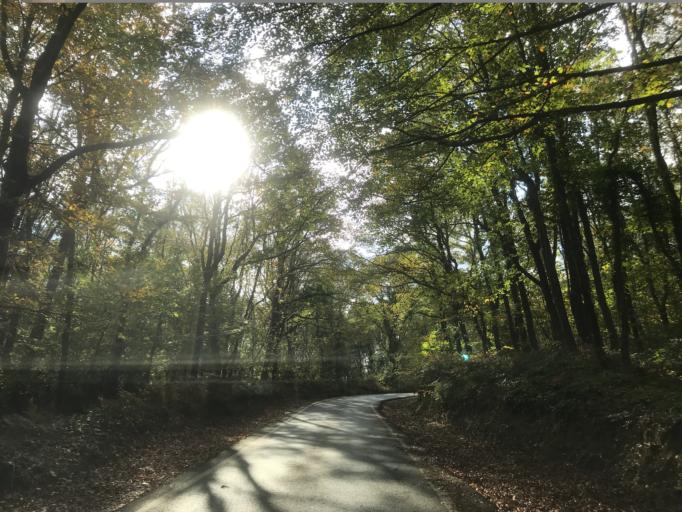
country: TR
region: Istanbul
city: Arikoey
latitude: 41.1849
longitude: 28.9873
